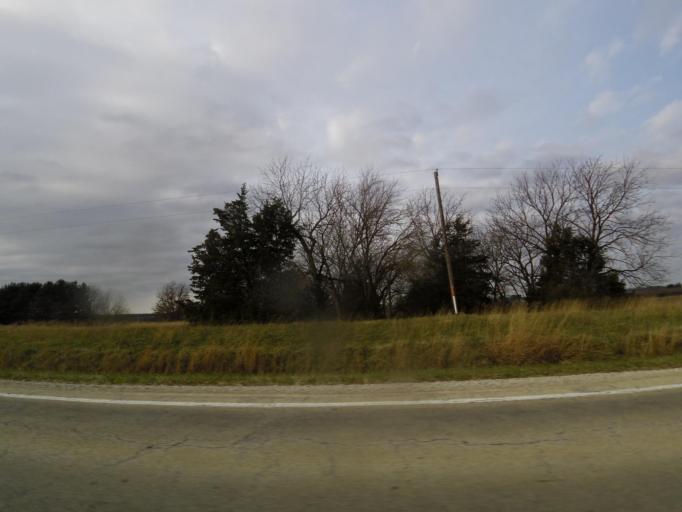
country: US
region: Illinois
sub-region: Christian County
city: Pana
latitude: 39.4068
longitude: -89.0441
